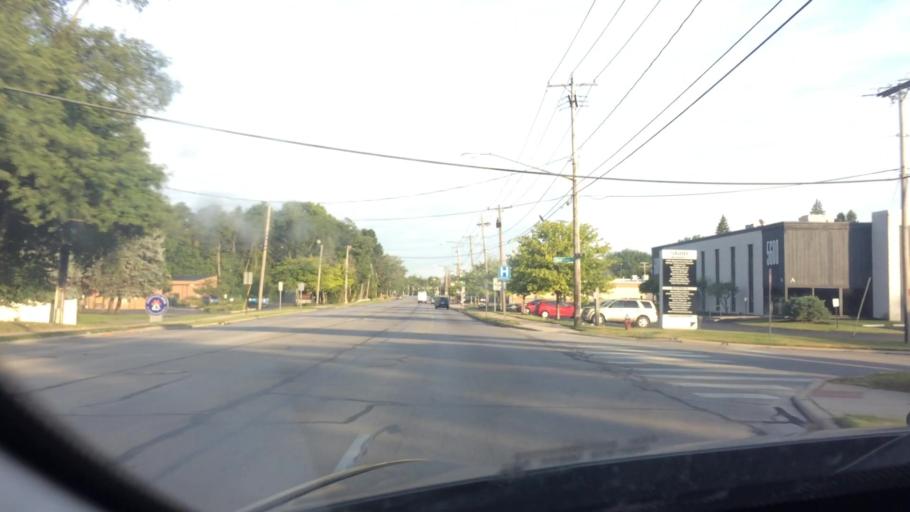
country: US
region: Ohio
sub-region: Lucas County
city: Sylvania
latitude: 41.7079
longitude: -83.6700
